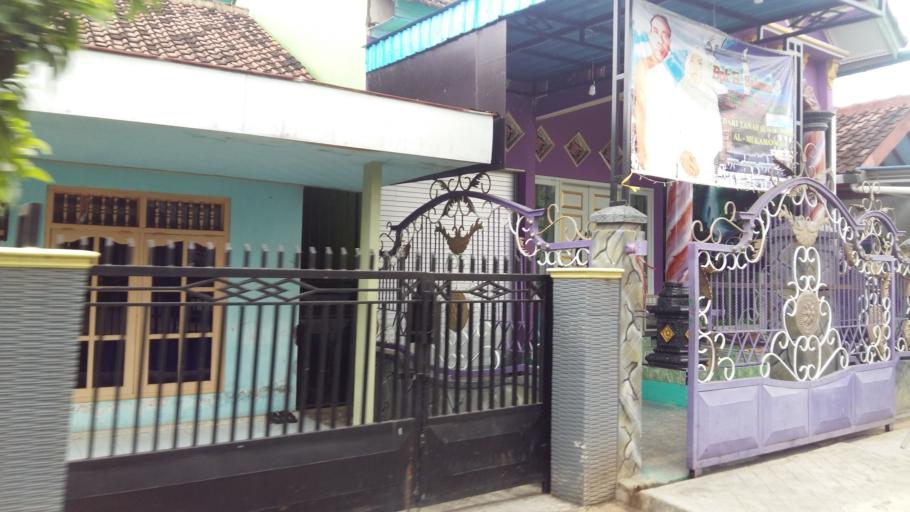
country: ID
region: East Java
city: Krajan
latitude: -8.3028
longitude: 114.2857
